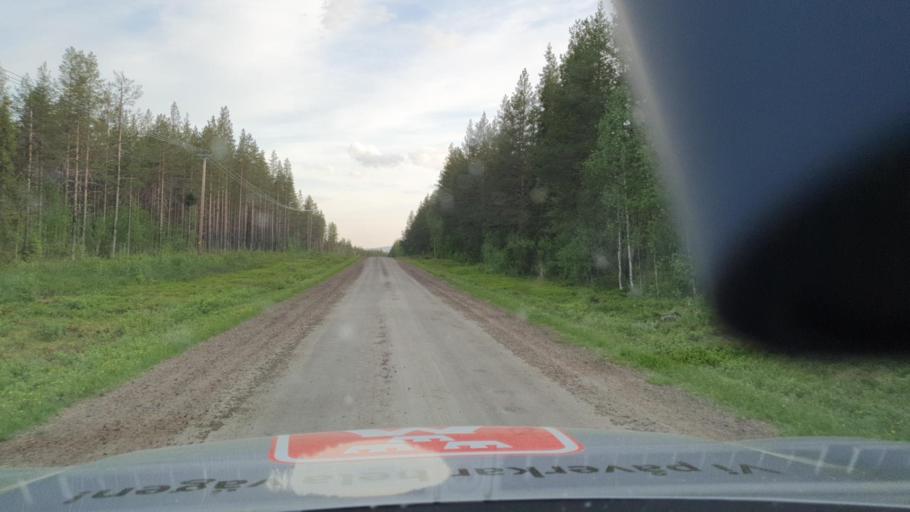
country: SE
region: Norrbotten
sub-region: Bodens Kommun
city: Boden
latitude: 66.3443
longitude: 21.4447
